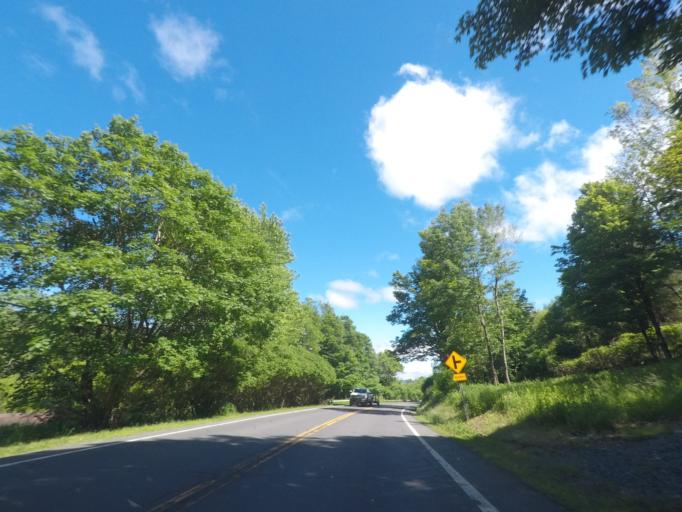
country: US
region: New York
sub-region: Columbia County
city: Philmont
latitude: 42.1942
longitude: -73.6234
